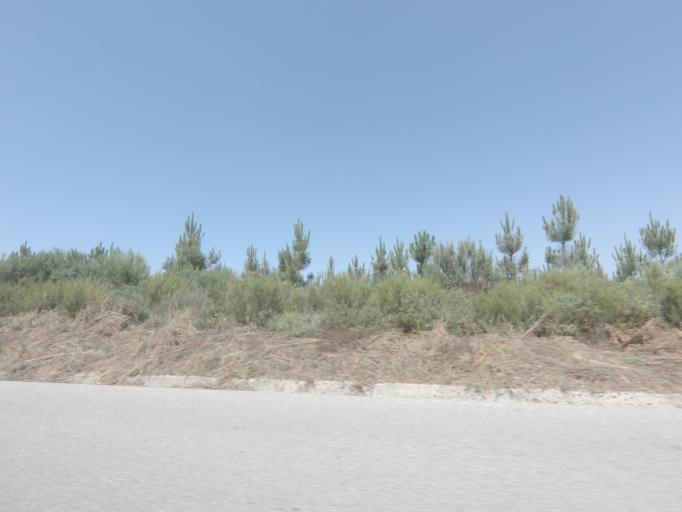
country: PT
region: Viseu
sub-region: Tarouca
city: Tarouca
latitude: 40.9906
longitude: -7.8352
